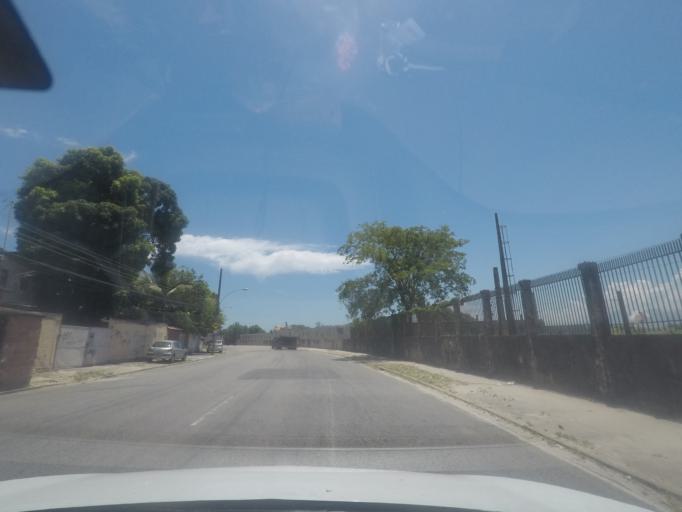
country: BR
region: Rio de Janeiro
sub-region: Itaguai
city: Itaguai
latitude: -22.9207
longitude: -43.6912
